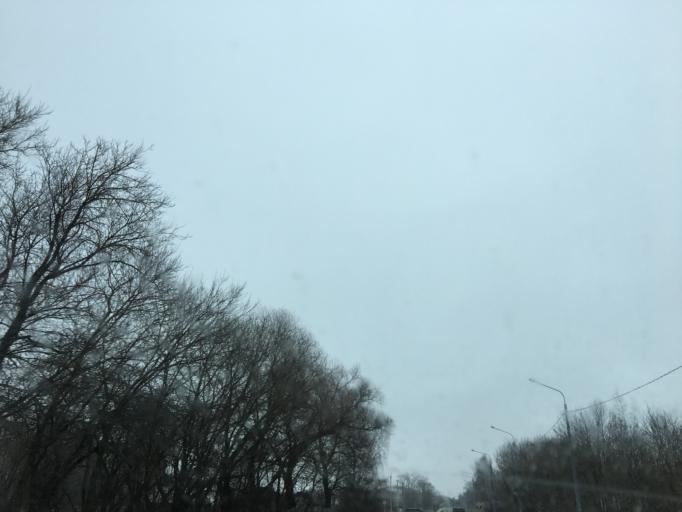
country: RU
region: Tula
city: Bolokhovo
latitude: 54.0530
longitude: 37.8126
